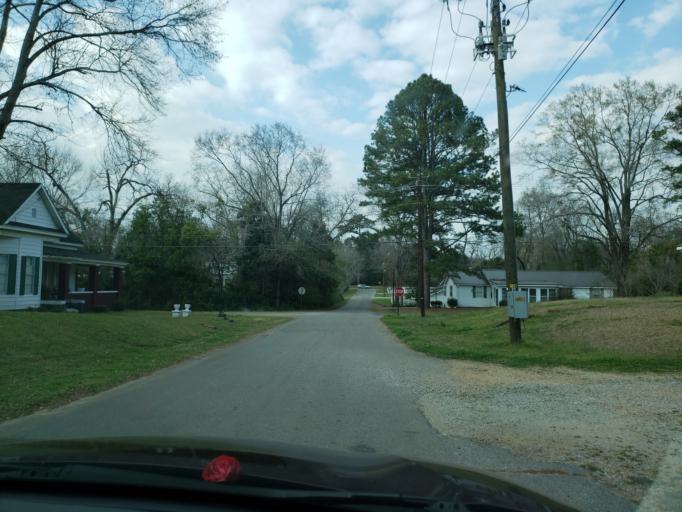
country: US
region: Alabama
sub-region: Hale County
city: Greensboro
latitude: 32.7024
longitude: -87.6054
